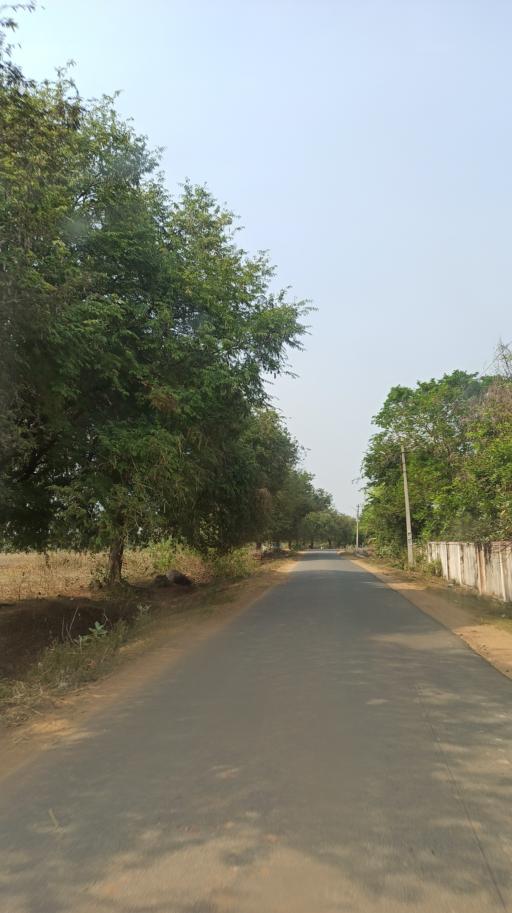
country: IN
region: Tamil Nadu
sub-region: Tiruvannamalai
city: Desur
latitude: 12.4573
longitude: 79.3725
